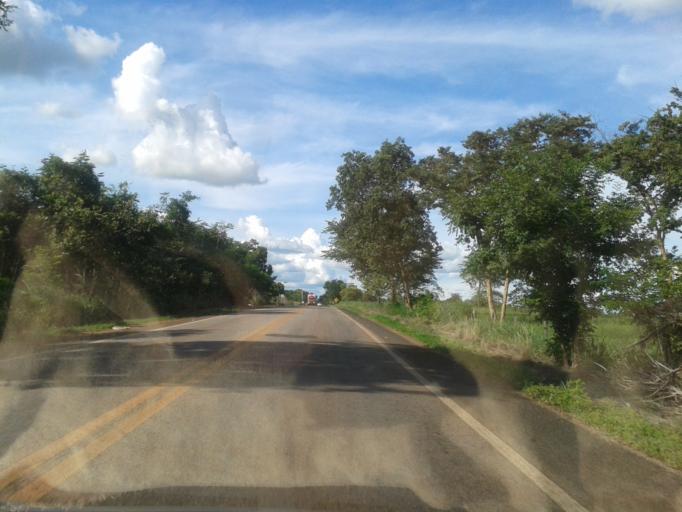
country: BR
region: Goias
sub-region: Mozarlandia
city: Mozarlandia
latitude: -14.6422
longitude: -50.5198
